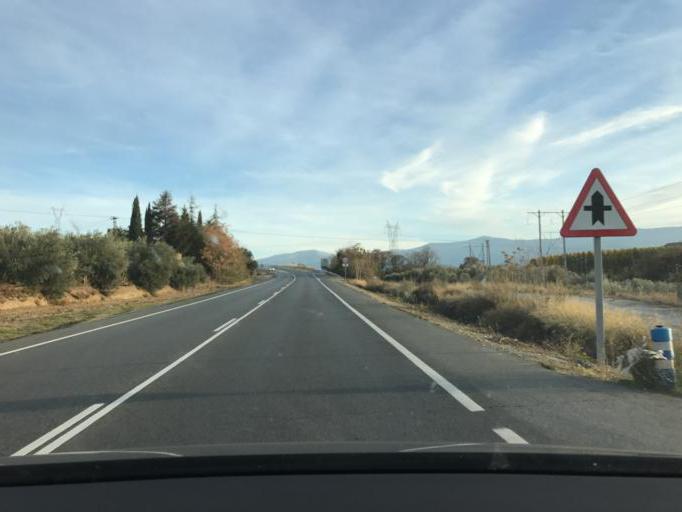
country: ES
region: Andalusia
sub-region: Provincia de Granada
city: Guadix
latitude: 37.2772
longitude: -3.1115
